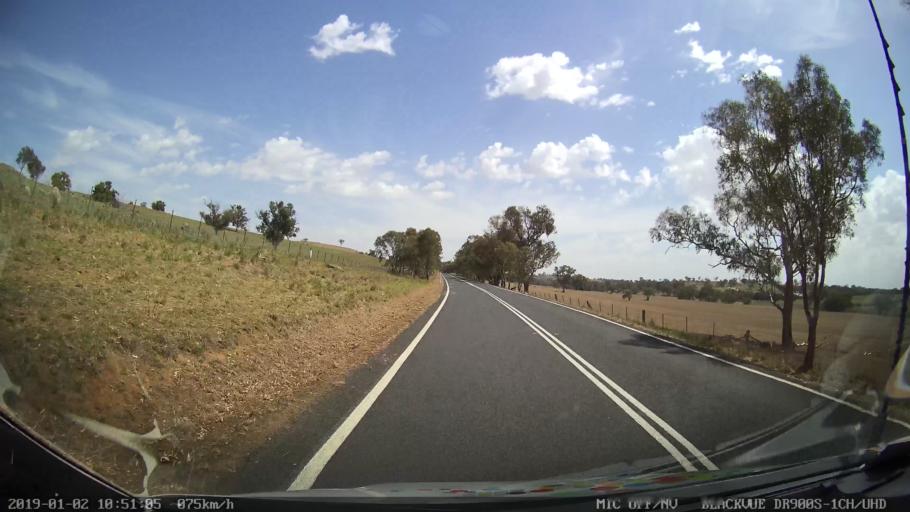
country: AU
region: New South Wales
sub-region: Cootamundra
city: Cootamundra
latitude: -34.7047
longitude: 148.2757
